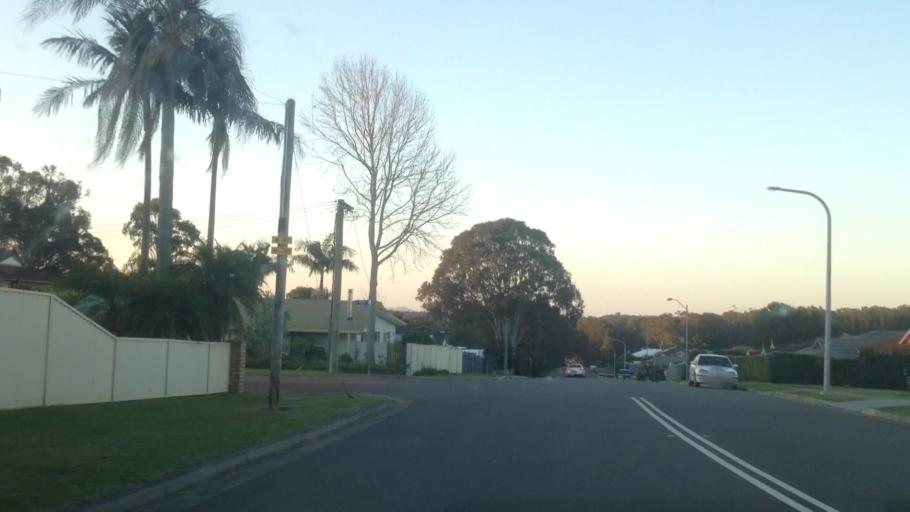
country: AU
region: New South Wales
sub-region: Wyong Shire
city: Kingfisher Shores
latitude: -33.1454
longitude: 151.5202
